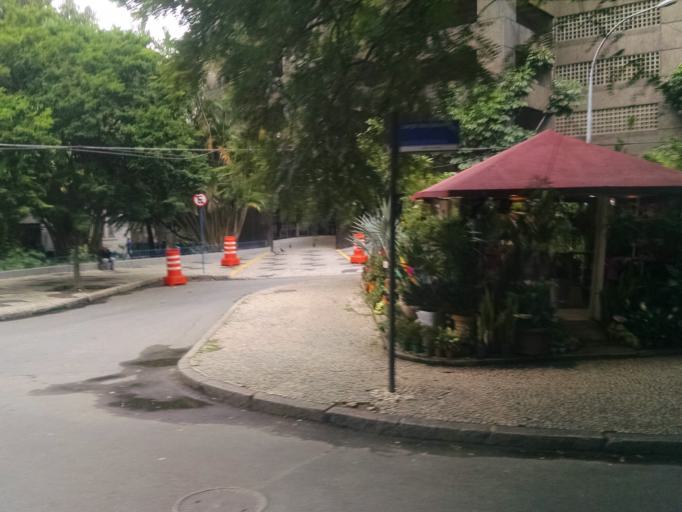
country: BR
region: Rio de Janeiro
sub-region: Rio De Janeiro
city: Rio de Janeiro
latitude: -22.9528
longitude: -43.1964
